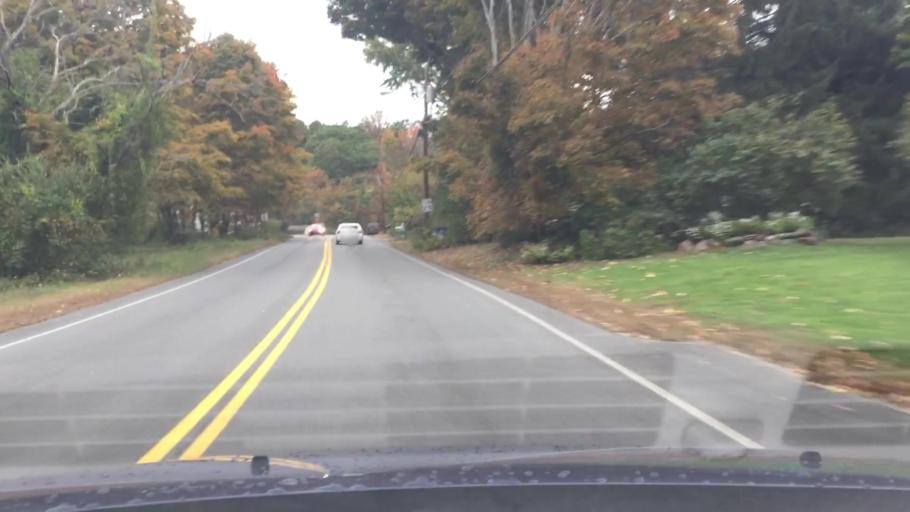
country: US
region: Massachusetts
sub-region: Middlesex County
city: Tyngsboro
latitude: 42.6917
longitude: -71.3831
